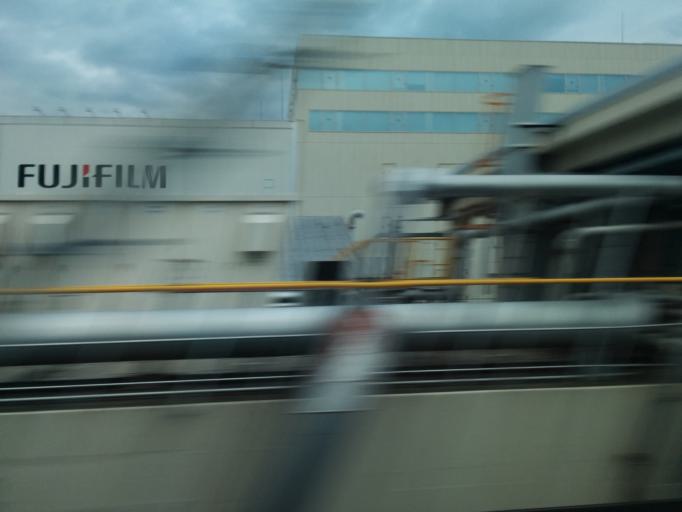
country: JP
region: Kanagawa
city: Odawara
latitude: 35.2662
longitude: 139.1646
